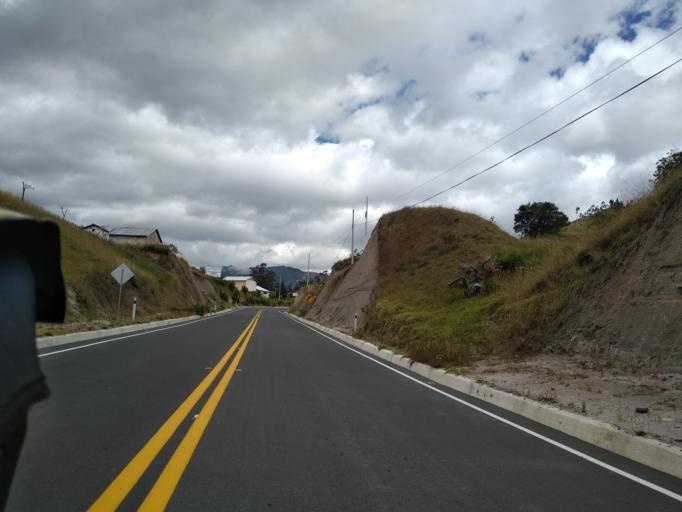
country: EC
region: Cotopaxi
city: Saquisili
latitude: -0.7854
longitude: -78.9132
